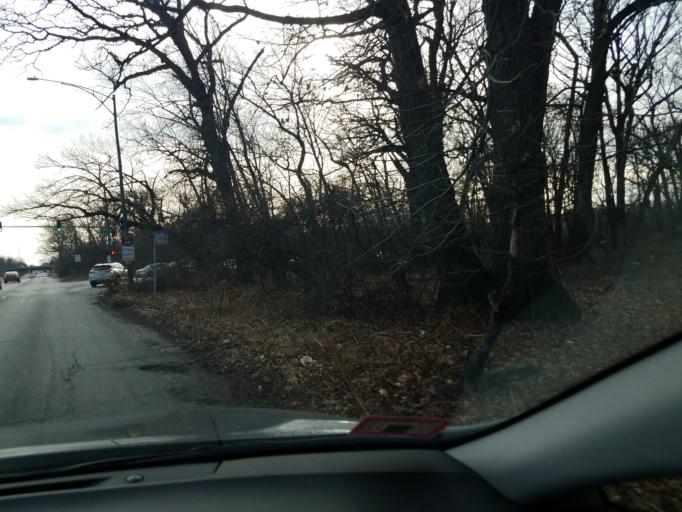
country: US
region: Illinois
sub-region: Cook County
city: Lincolnwood
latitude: 41.9860
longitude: -87.7484
